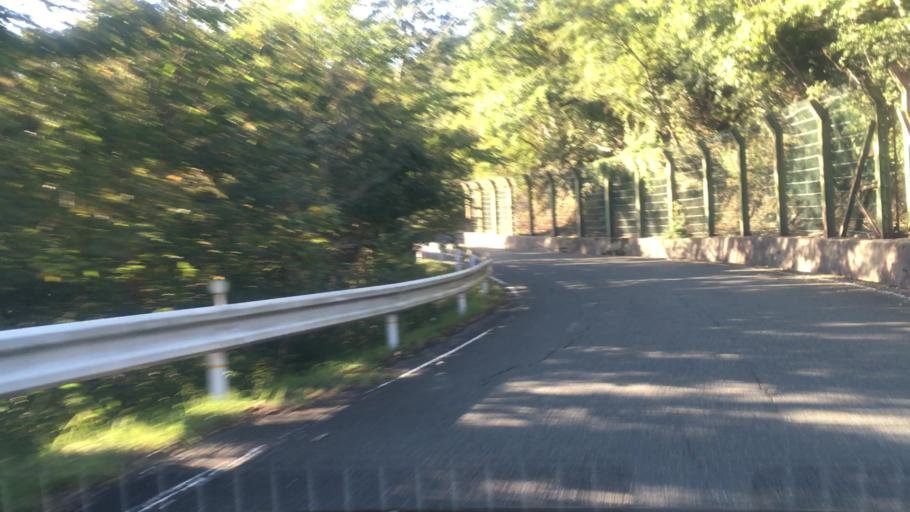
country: JP
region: Hyogo
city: Toyooka
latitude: 35.6140
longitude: 134.8790
